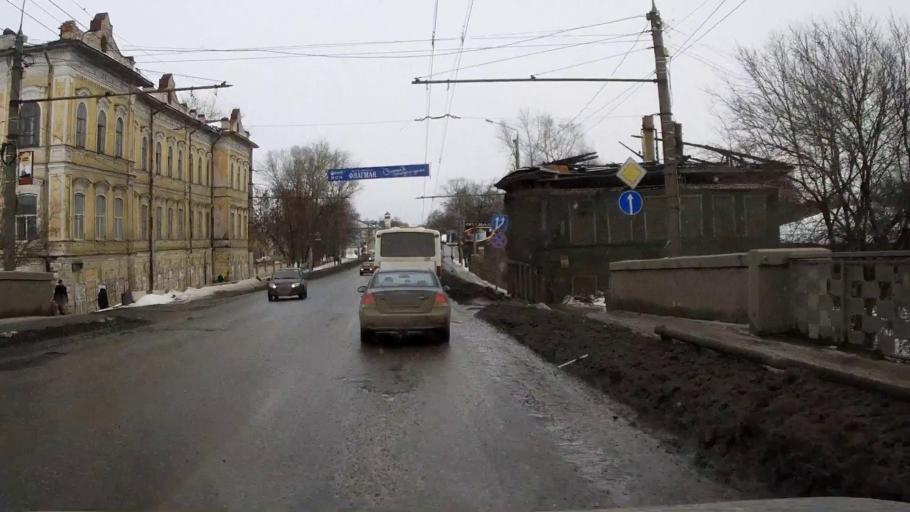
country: RU
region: Vologda
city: Vologda
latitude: 59.2243
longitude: 39.8916
